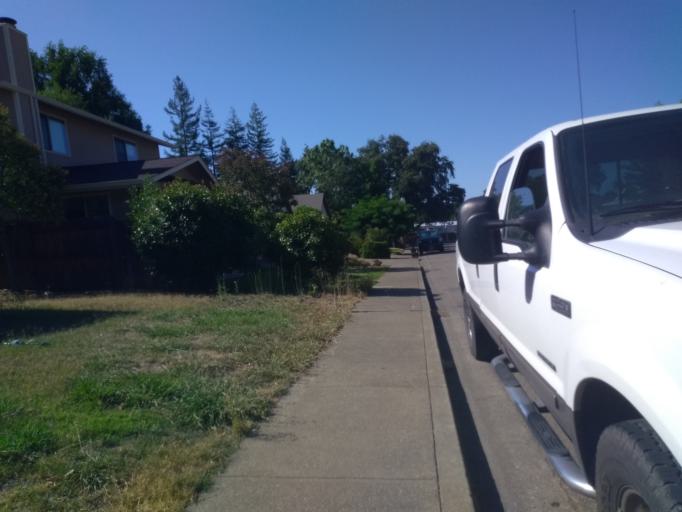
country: US
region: California
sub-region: Mendocino County
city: Ukiah
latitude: 39.1308
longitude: -123.2116
